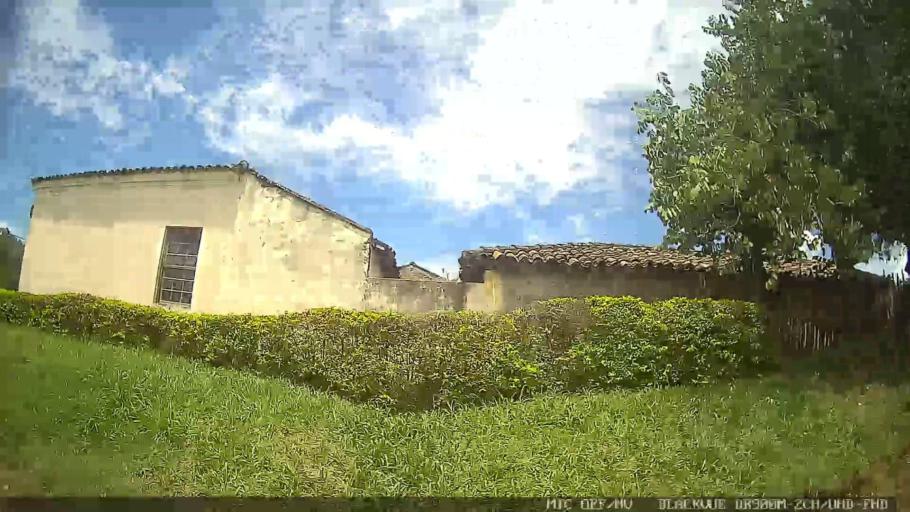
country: BR
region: Sao Paulo
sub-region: Conchas
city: Conchas
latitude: -23.0797
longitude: -47.9759
